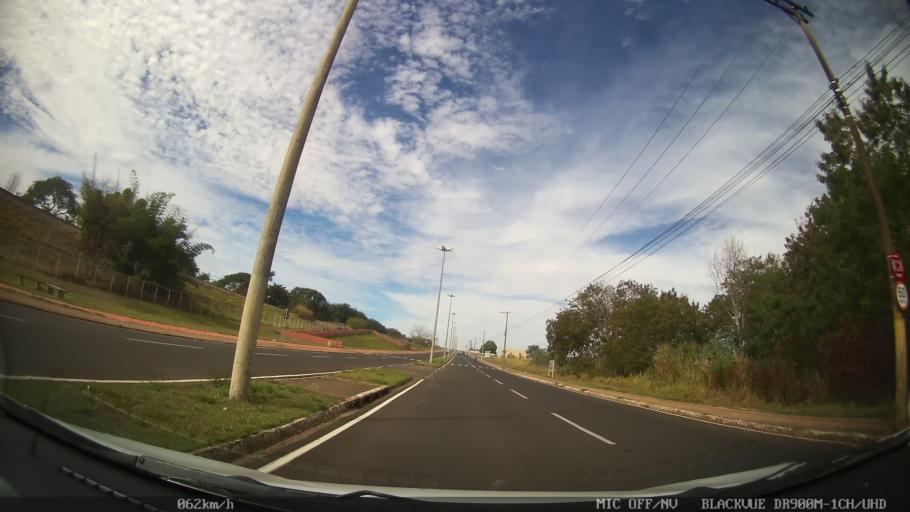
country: BR
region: Sao Paulo
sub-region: Catanduva
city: Catanduva
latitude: -21.1445
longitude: -48.9514
